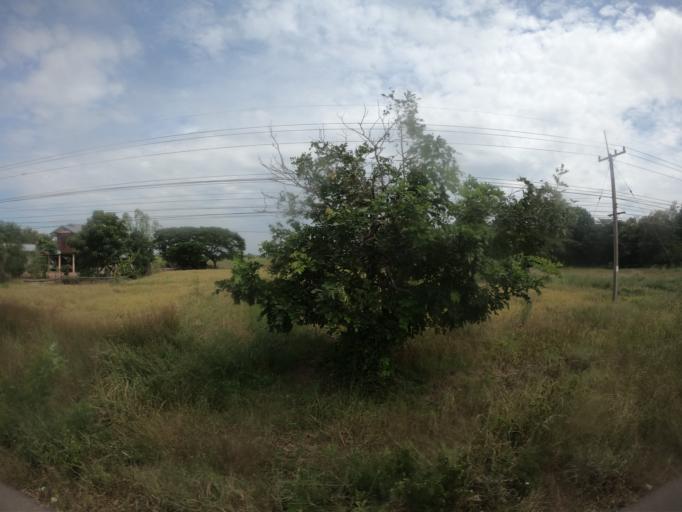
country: TH
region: Maha Sarakham
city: Chiang Yuen
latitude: 16.3548
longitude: 103.1159
